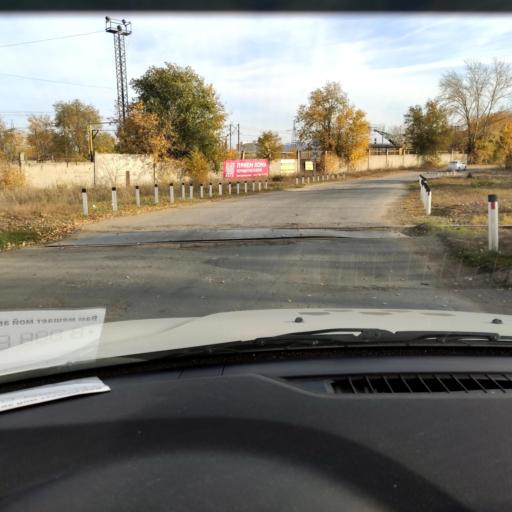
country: RU
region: Samara
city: Zhigulevsk
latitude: 53.4748
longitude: 49.5005
